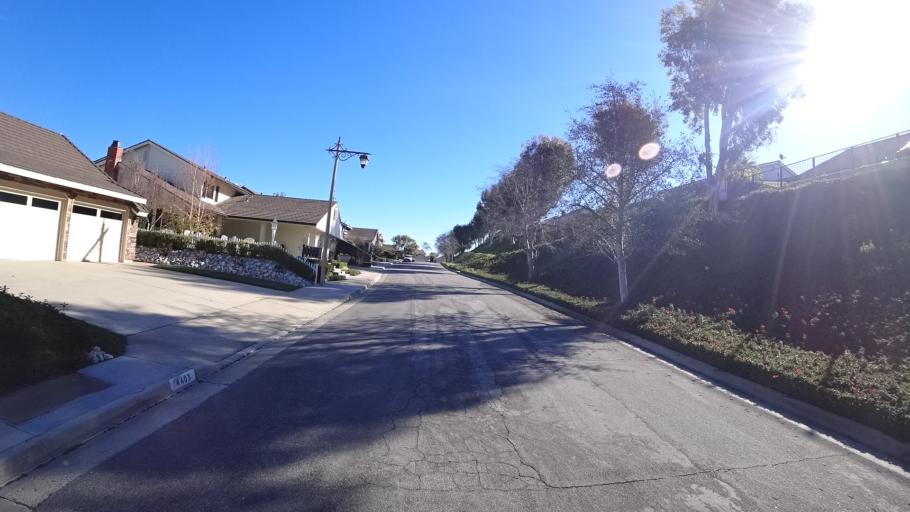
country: US
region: California
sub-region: Orange County
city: Villa Park
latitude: 33.8404
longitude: -117.8213
